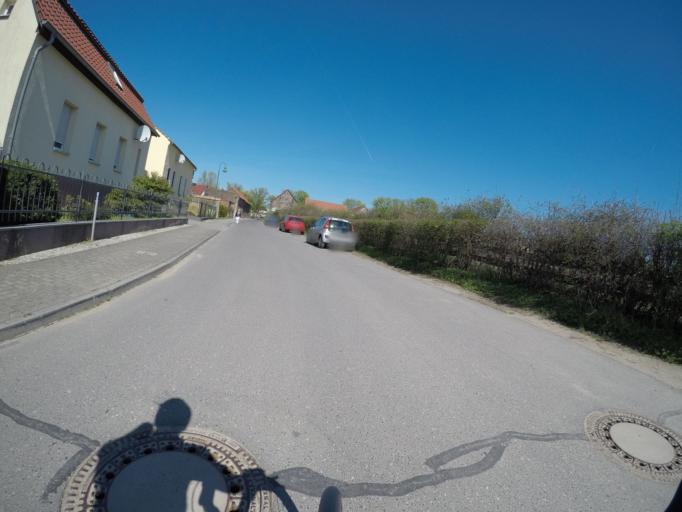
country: DE
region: Brandenburg
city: Werftpfuhl
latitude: 52.6387
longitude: 13.7929
